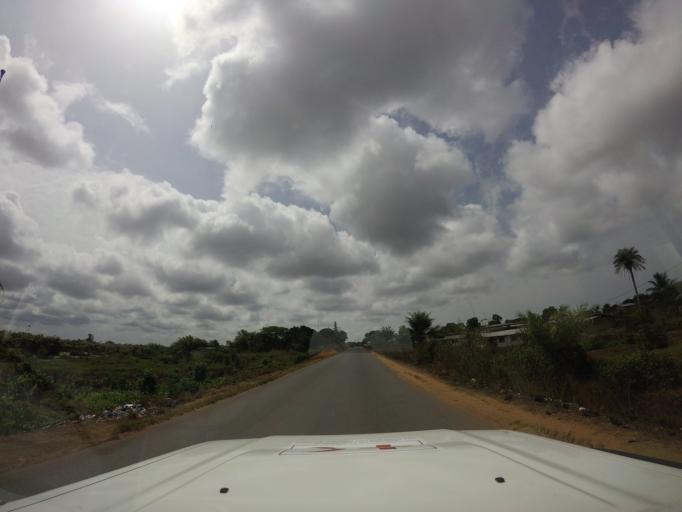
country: LR
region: Montserrado
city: Monrovia
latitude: 6.4595
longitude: -10.8056
